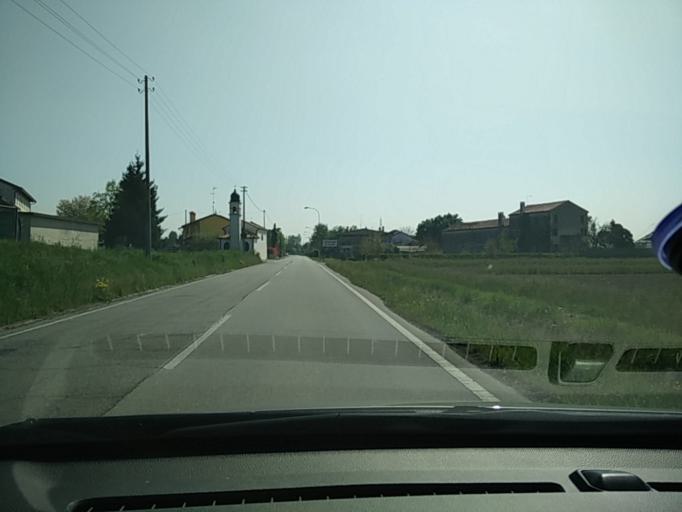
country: IT
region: Veneto
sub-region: Provincia di Treviso
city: Zenson di Piave
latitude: 45.6764
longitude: 12.4738
